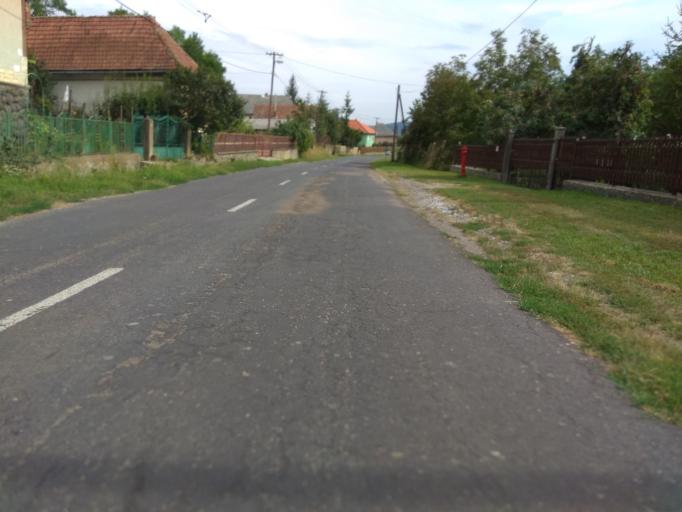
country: HU
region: Heves
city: Tarnalelesz
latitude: 48.0301
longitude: 20.2562
